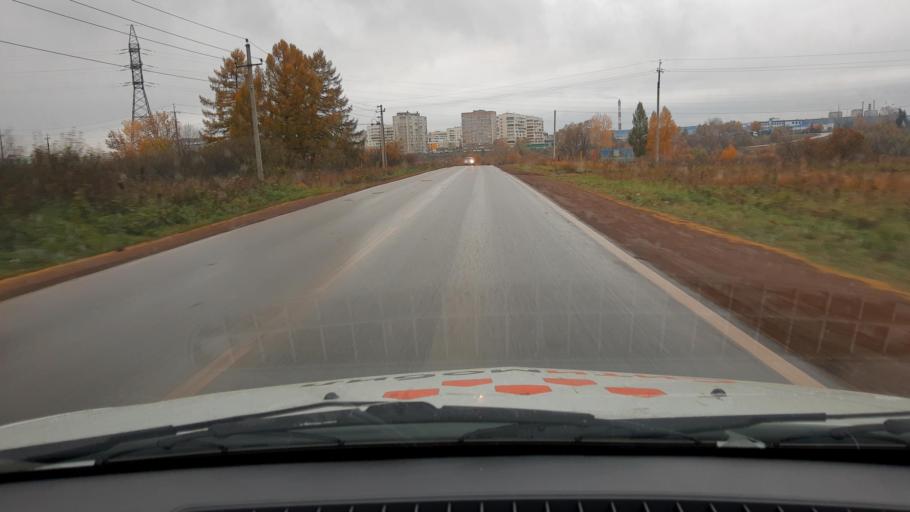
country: RU
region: Bashkortostan
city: Iglino
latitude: 54.7495
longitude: 56.2509
